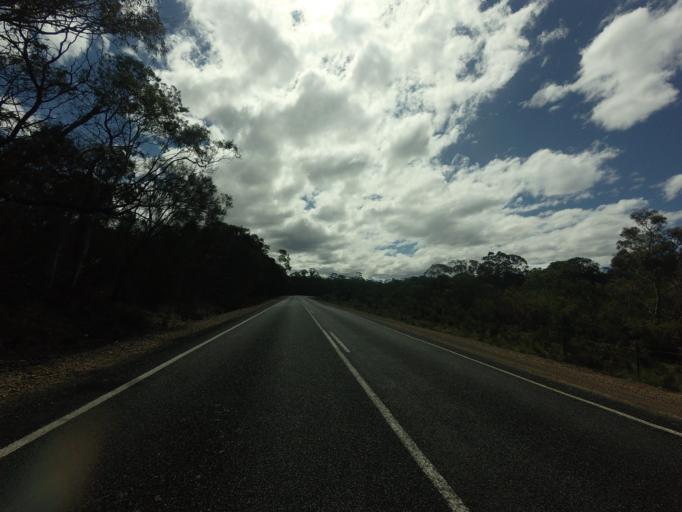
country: AU
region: Tasmania
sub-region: Break O'Day
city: St Helens
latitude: -42.0222
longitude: 148.0089
